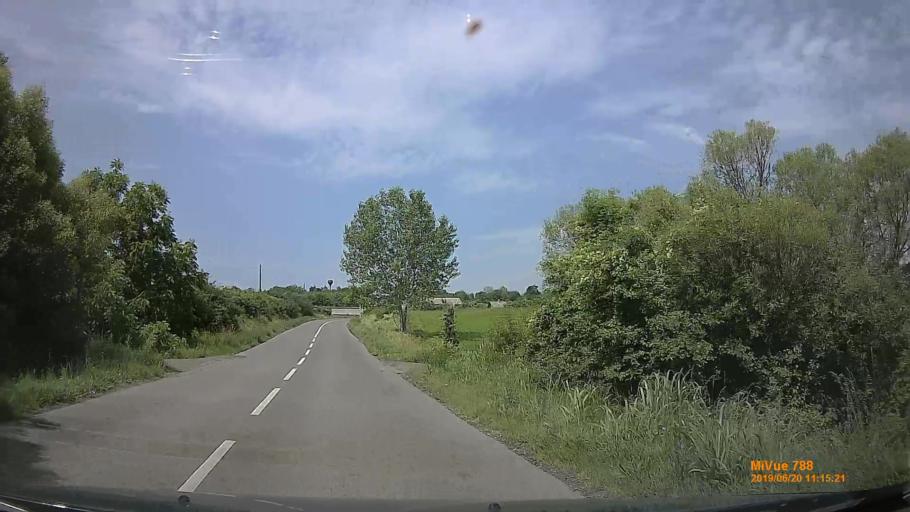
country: HU
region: Baranya
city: Pecsvarad
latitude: 46.1505
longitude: 18.4889
